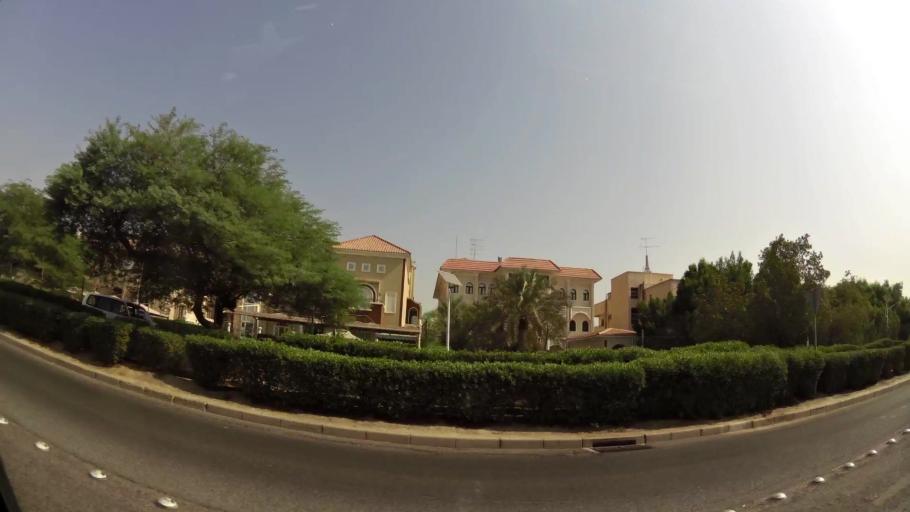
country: KW
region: Al Asimah
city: Ad Dasmah
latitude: 29.3575
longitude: 47.9895
